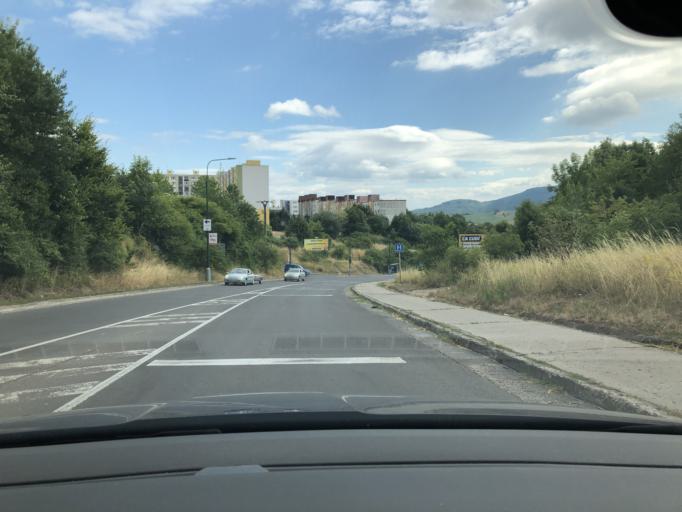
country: SK
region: Banskobystricky
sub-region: Okres Banska Bystrica
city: Banska Stiavnica
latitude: 48.4552
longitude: 18.9154
